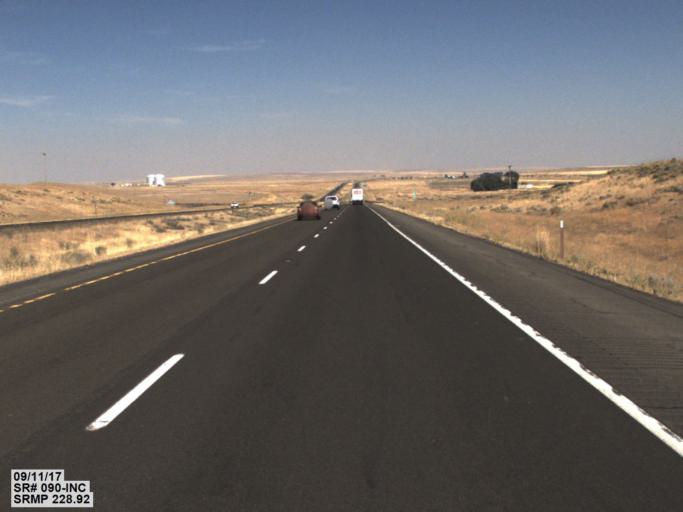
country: US
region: Washington
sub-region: Adams County
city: Ritzville
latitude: 47.1883
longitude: -118.2624
